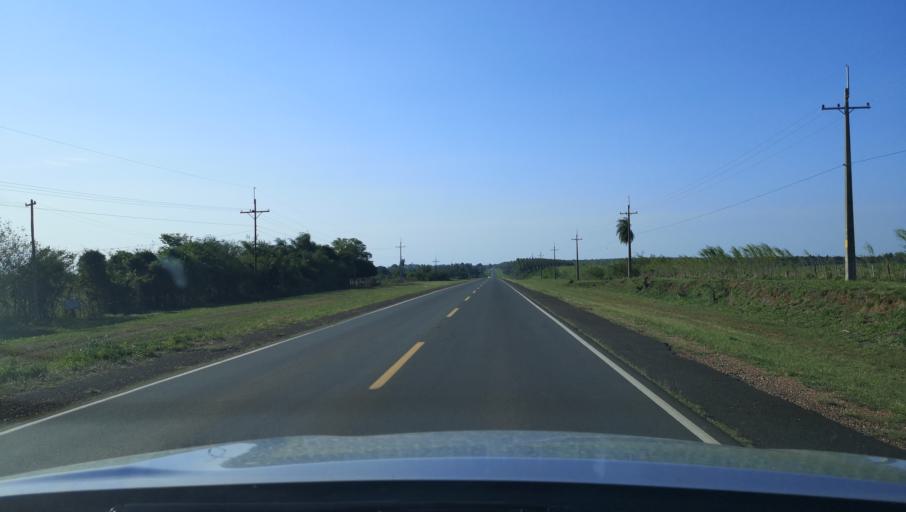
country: PY
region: Misiones
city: Santa Maria
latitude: -26.7806
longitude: -57.0277
